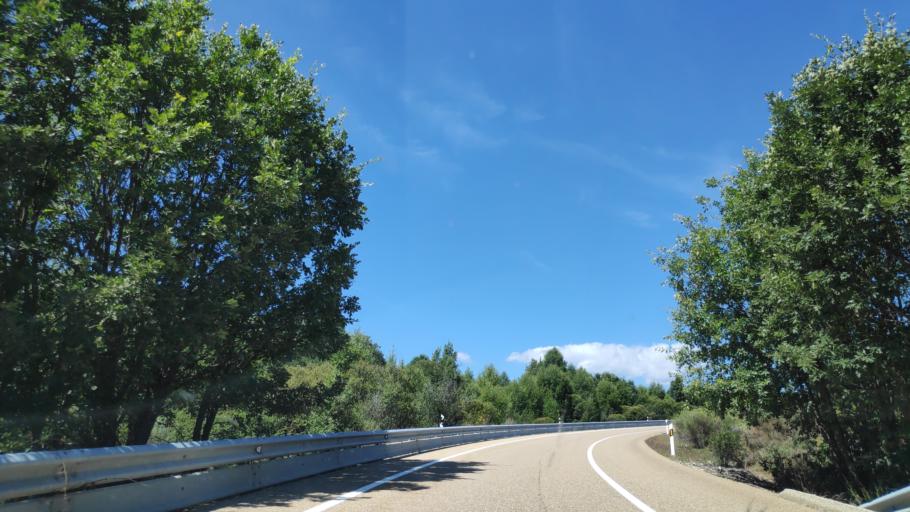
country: ES
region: Castille and Leon
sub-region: Provincia de Zamora
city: Puebla de Sanabria
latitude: 42.0565
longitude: -6.6667
